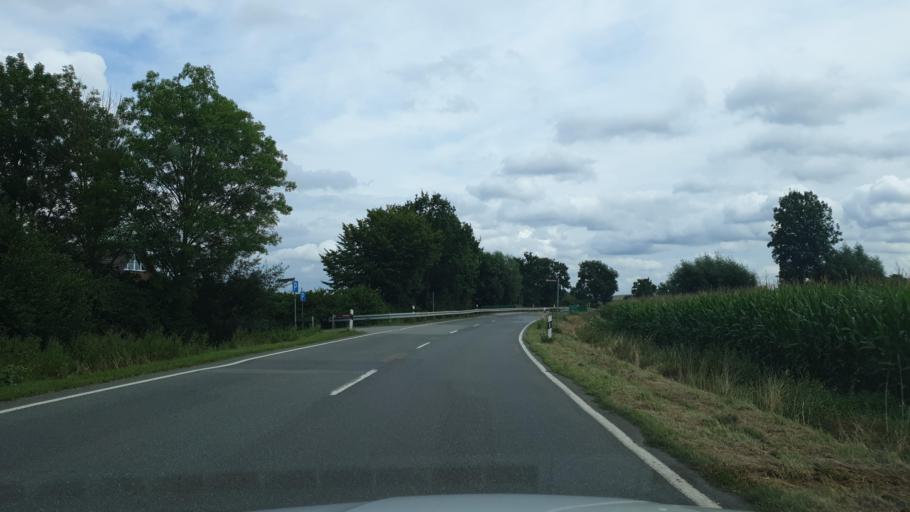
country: DE
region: Lower Saxony
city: Melle
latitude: 52.1980
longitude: 8.2545
